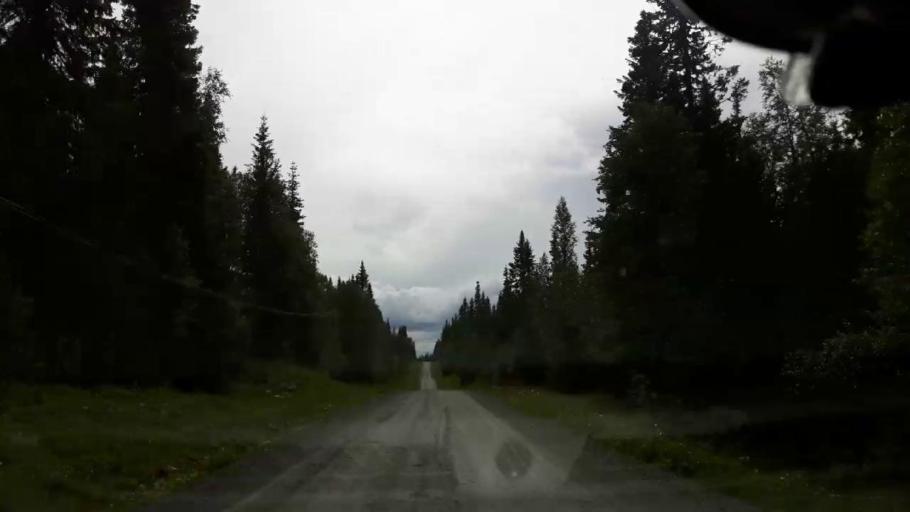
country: SE
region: Jaemtland
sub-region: Krokoms Kommun
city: Valla
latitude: 63.7469
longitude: 13.8355
